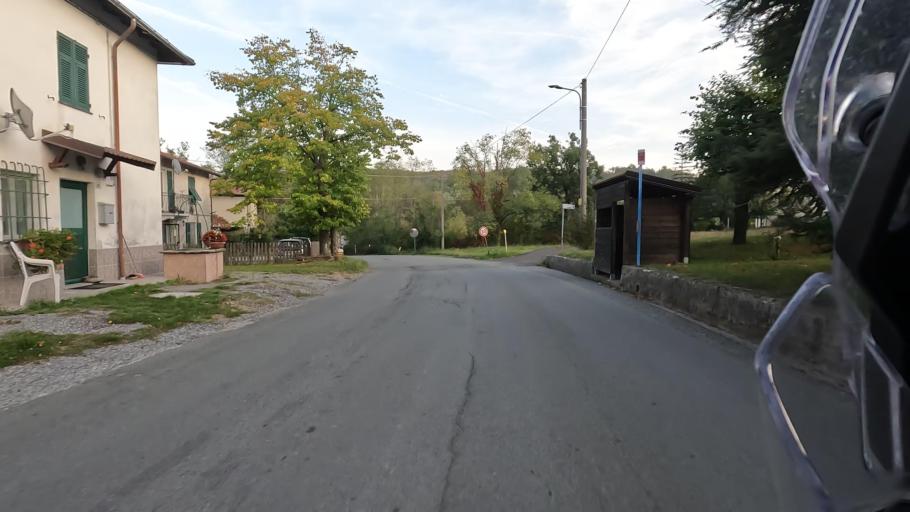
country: IT
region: Liguria
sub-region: Provincia di Savona
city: Mioglia
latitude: 44.4702
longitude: 8.4176
